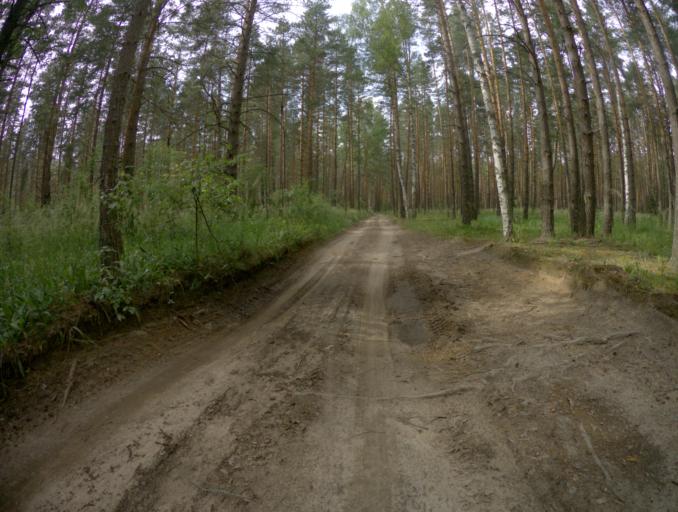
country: RU
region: Nizjnij Novgorod
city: Frolishchi
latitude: 56.3113
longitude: 42.6606
